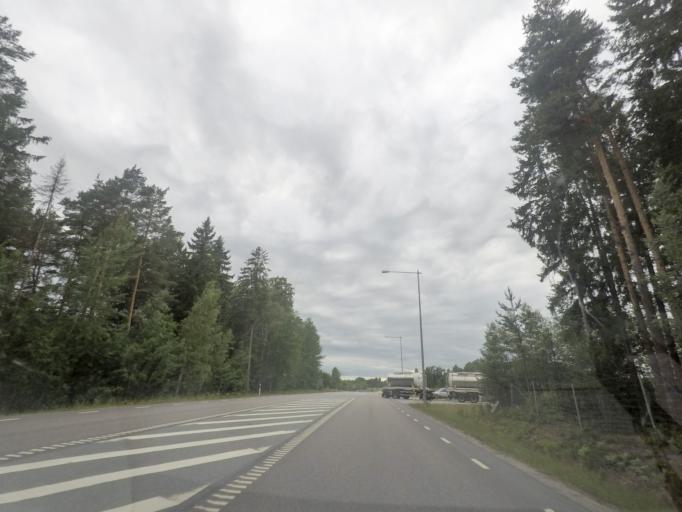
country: SE
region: Vaestmanland
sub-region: Arboga Kommun
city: Arboga
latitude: 59.4120
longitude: 15.7730
